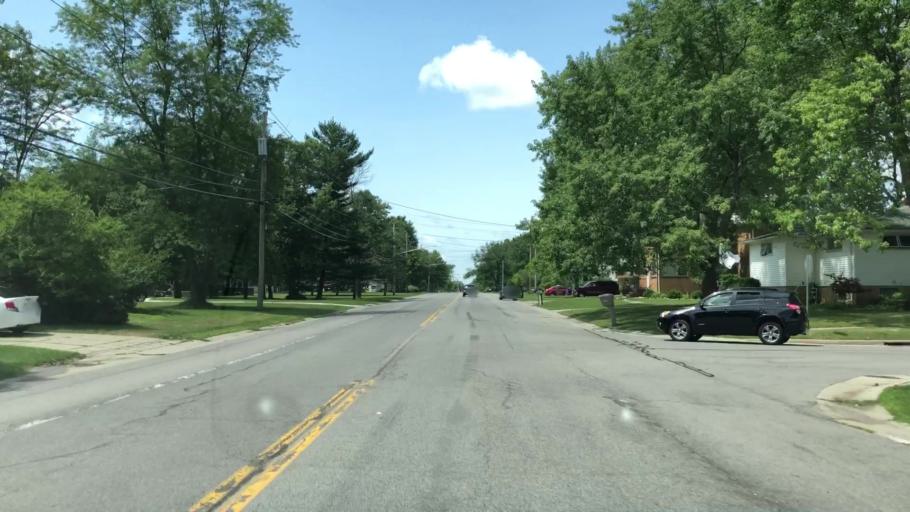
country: US
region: New York
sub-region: Erie County
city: Orchard Park
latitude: 42.8113
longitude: -78.7288
